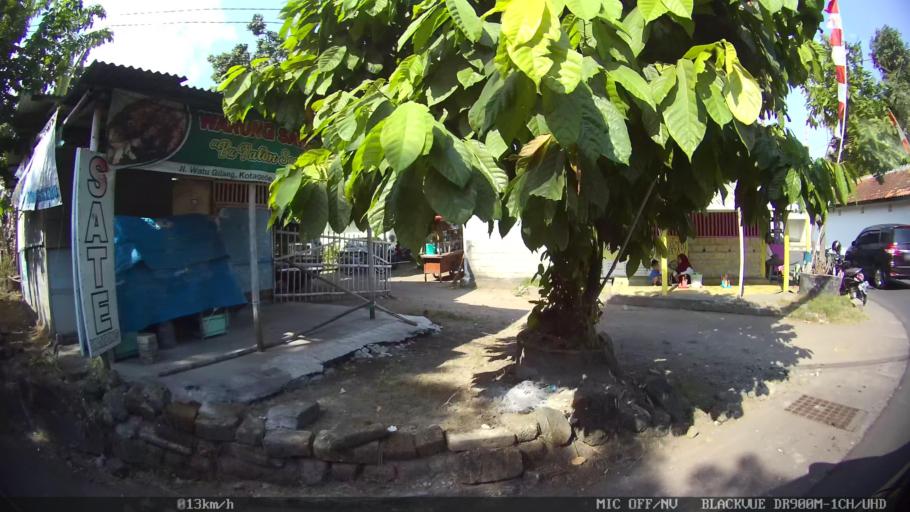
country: ID
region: Daerah Istimewa Yogyakarta
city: Sewon
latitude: -7.8316
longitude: 110.3990
